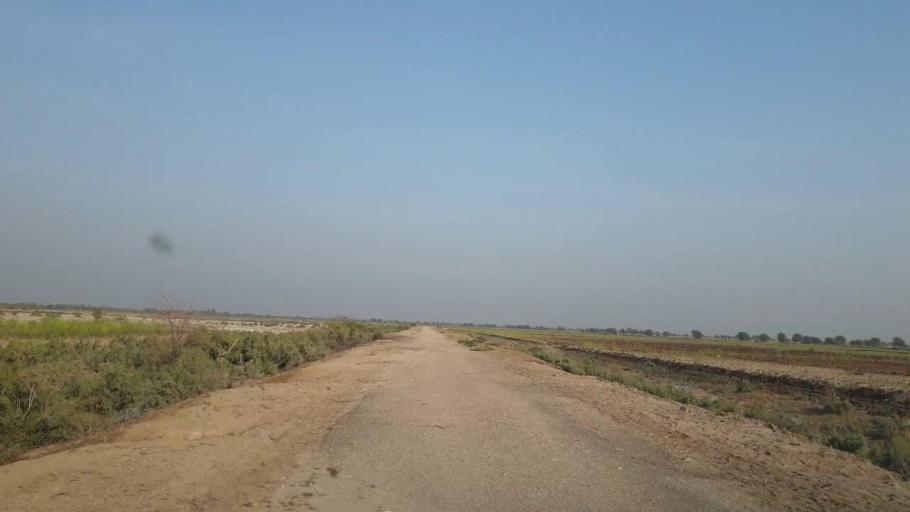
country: PK
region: Sindh
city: Mirpur Khas
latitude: 25.6698
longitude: 69.1976
